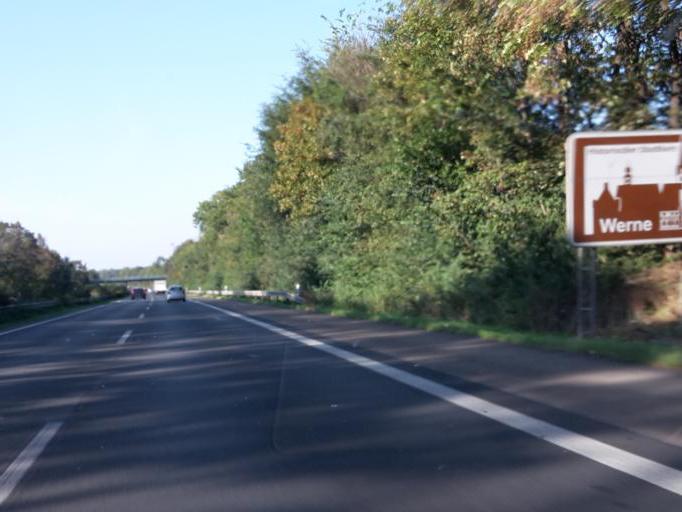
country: DE
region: North Rhine-Westphalia
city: Werne
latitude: 51.6808
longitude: 7.6776
